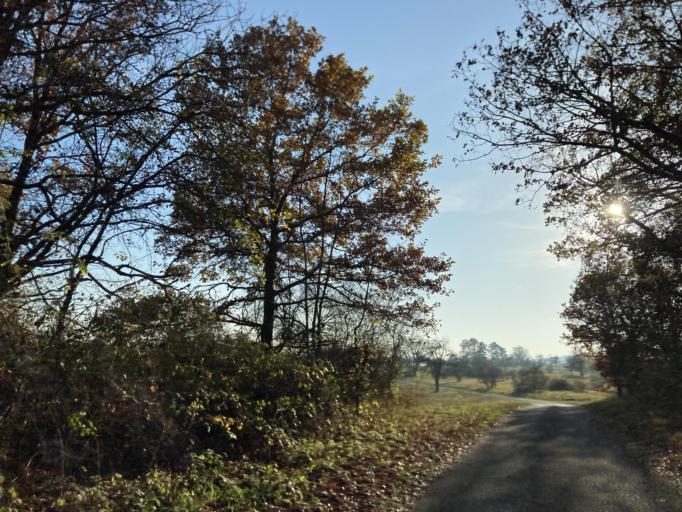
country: DE
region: Baden-Wuerttemberg
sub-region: Tuebingen Region
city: Rottenburg
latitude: 48.5391
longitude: 8.9753
